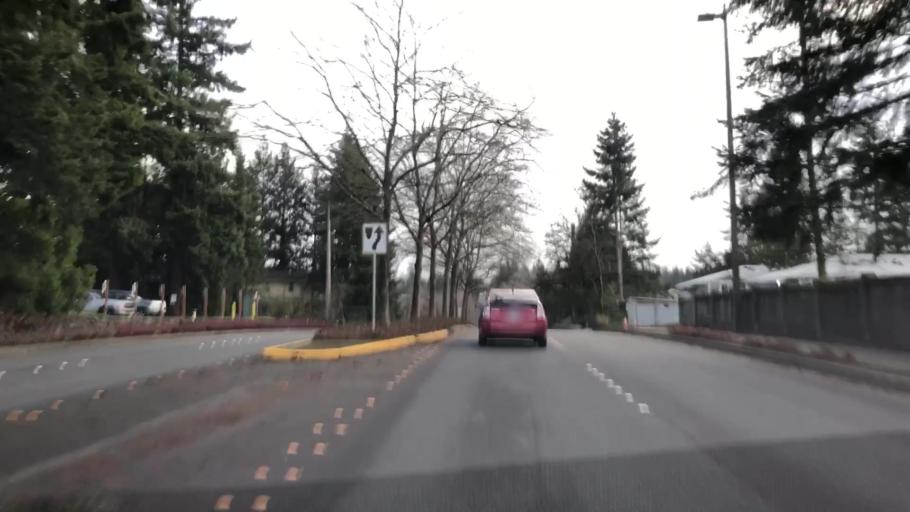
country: US
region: Washington
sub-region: King County
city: Eastgate
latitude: 47.6171
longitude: -122.1467
